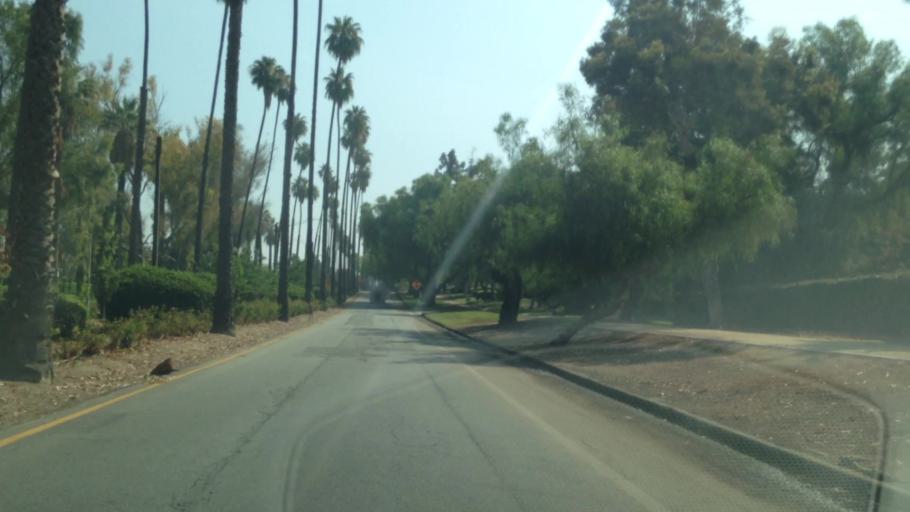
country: US
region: California
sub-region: Riverside County
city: Riverside
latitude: 33.9329
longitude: -117.3839
